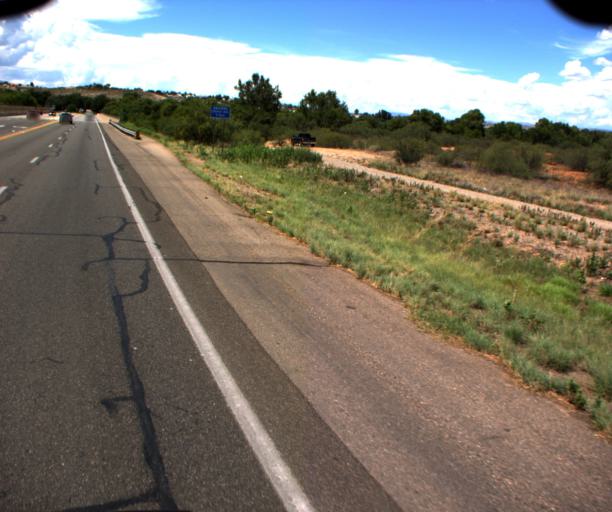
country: US
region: Arizona
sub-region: Yavapai County
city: Camp Verde
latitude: 34.5494
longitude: -111.8496
